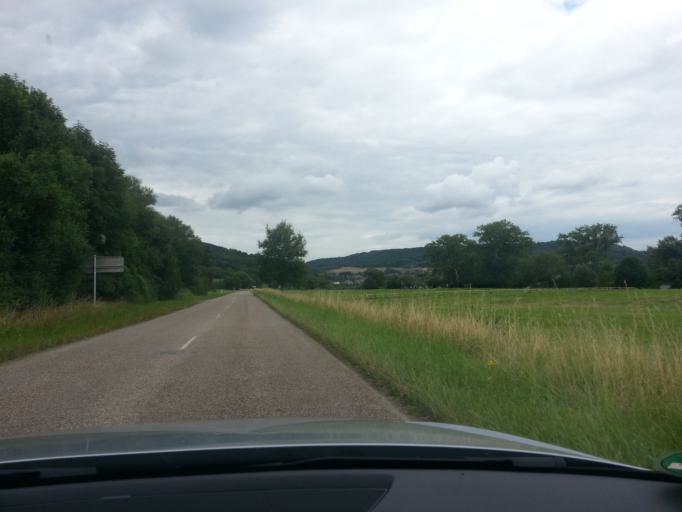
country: FR
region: Lorraine
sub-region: Departement de la Moselle
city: Sierck-les-Bains
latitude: 49.4483
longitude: 6.3227
